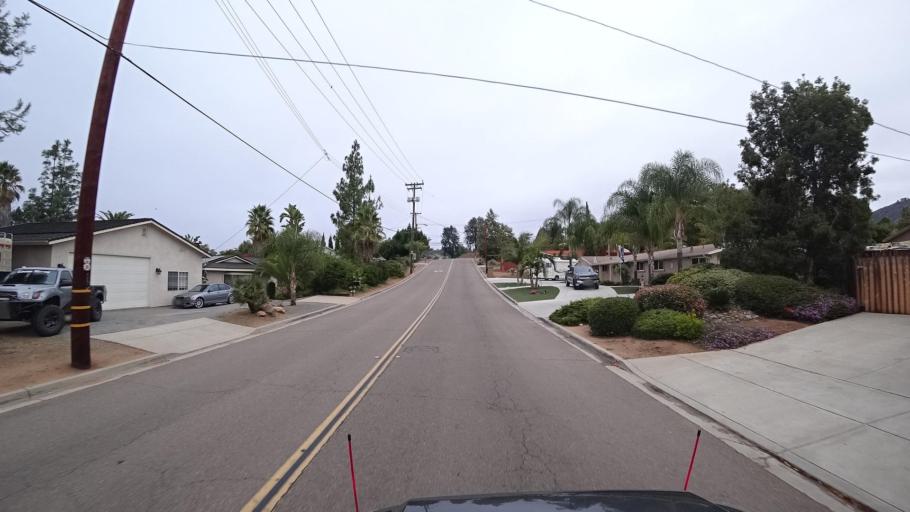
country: US
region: California
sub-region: San Diego County
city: Rancho San Diego
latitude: 32.7610
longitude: -116.9177
